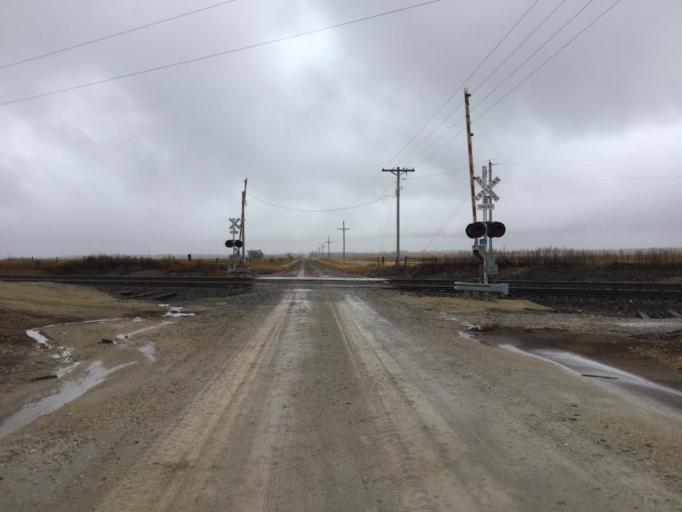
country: US
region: Kansas
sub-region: Butler County
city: El Dorado
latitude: 37.9850
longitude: -96.6861
